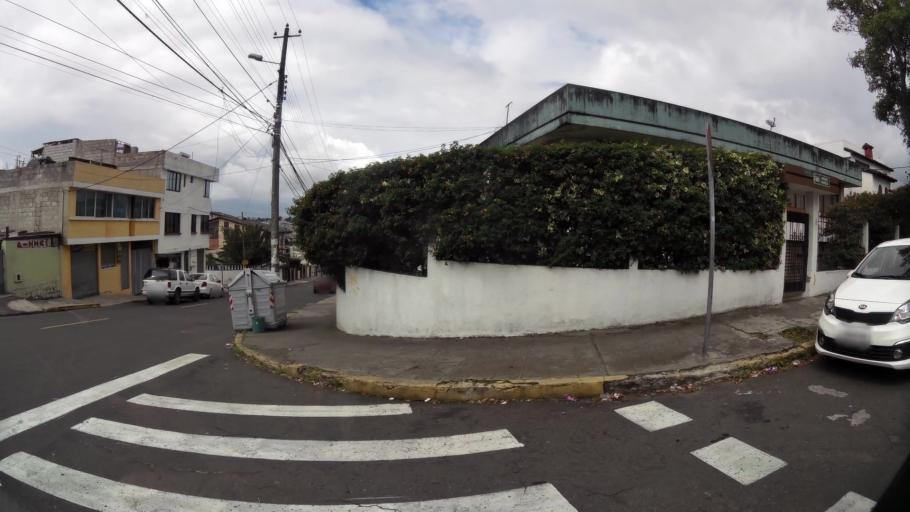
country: EC
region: Pichincha
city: Quito
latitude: -0.1483
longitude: -78.4973
